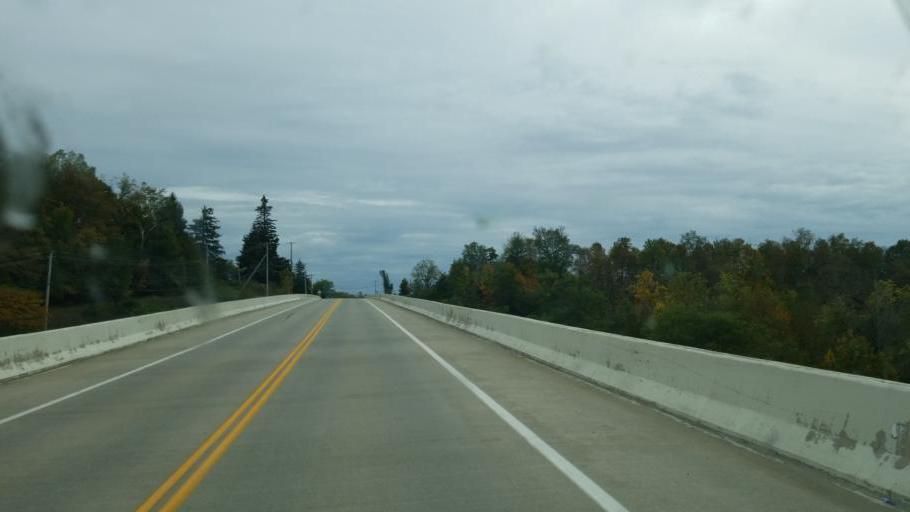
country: US
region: Ohio
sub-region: Huron County
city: Wakeman
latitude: 41.3162
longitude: -82.3644
